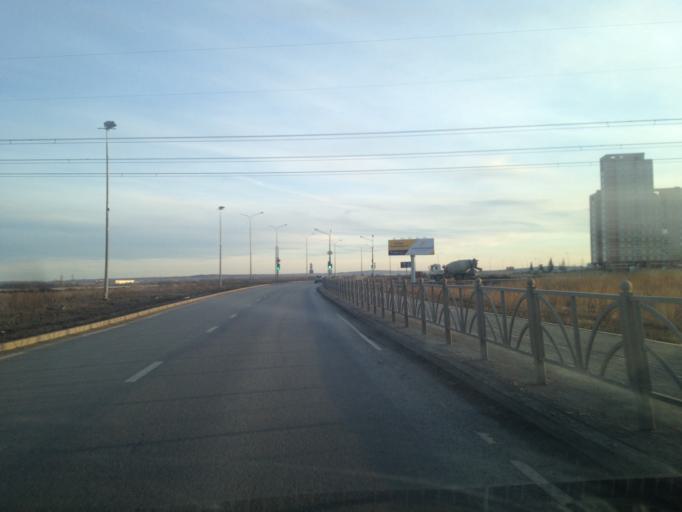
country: RU
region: Sverdlovsk
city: Sovkhoznyy
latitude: 56.7477
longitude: 60.5754
